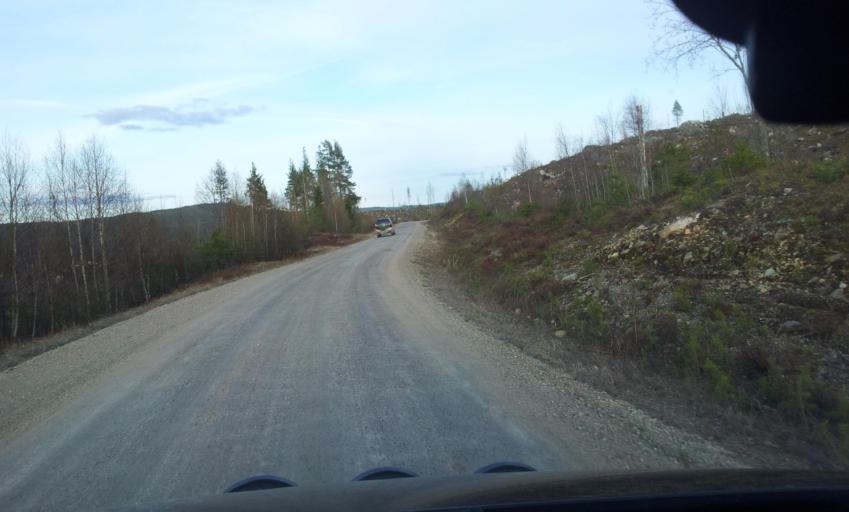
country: SE
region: Gaevleborg
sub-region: Ljusdals Kommun
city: Farila
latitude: 62.1122
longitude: 15.7071
